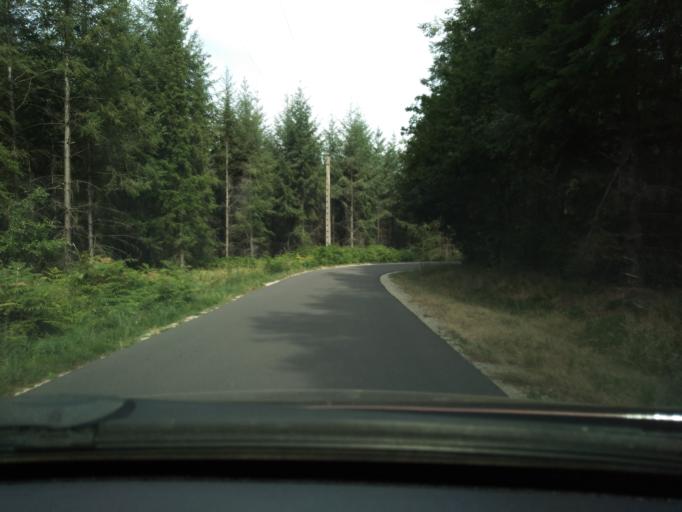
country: FR
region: Bourgogne
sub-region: Departement de la Cote-d'Or
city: Saulieu
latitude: 47.3719
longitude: 4.0829
